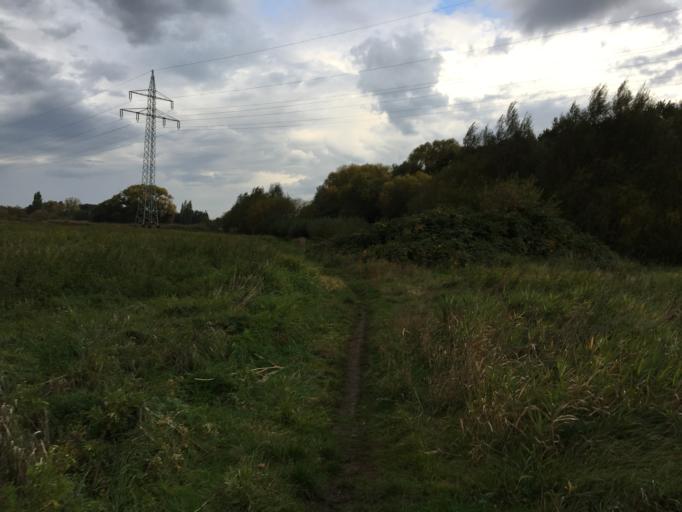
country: DE
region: Lower Saxony
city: Braunschweig
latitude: 52.2985
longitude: 10.5311
